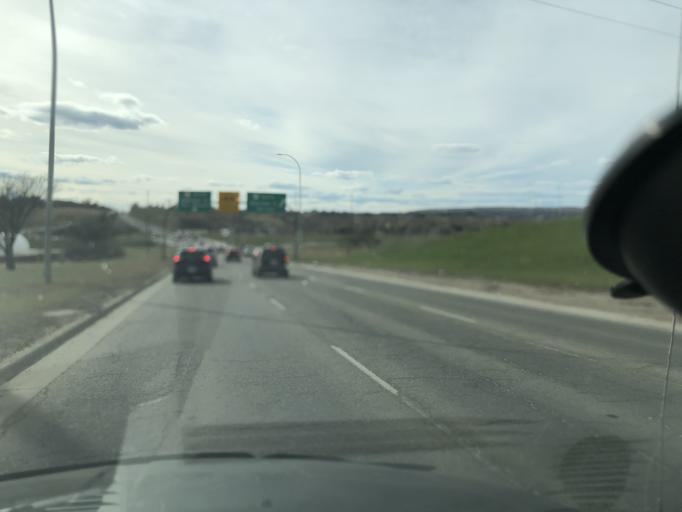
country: CA
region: Alberta
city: Calgary
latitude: 51.0672
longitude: -114.0224
